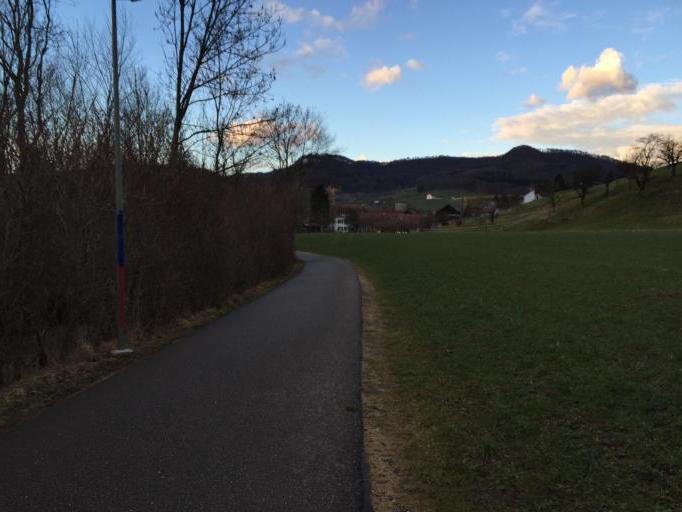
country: CH
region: Basel-Landschaft
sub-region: Bezirk Sissach
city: Zunzgen
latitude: 47.4557
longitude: 7.8090
